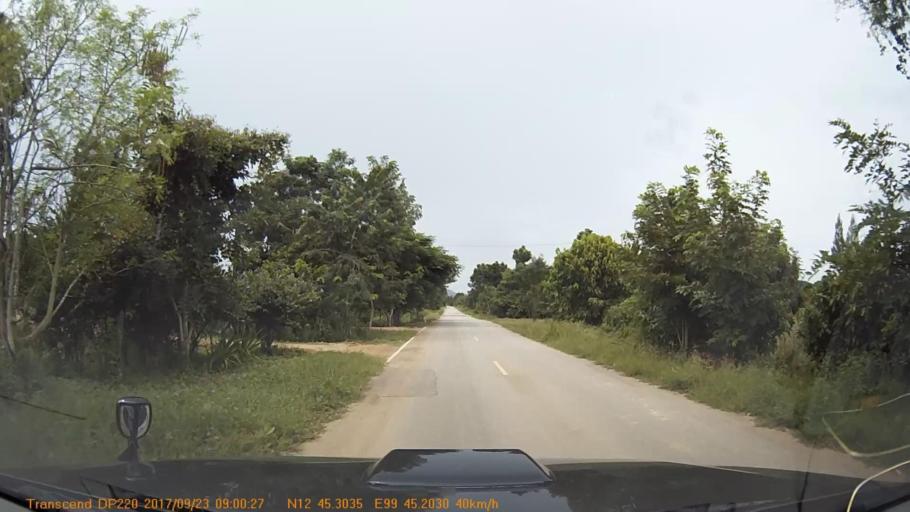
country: TH
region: Phetchaburi
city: Kaeng Krachan
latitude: 12.7551
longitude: 99.7534
